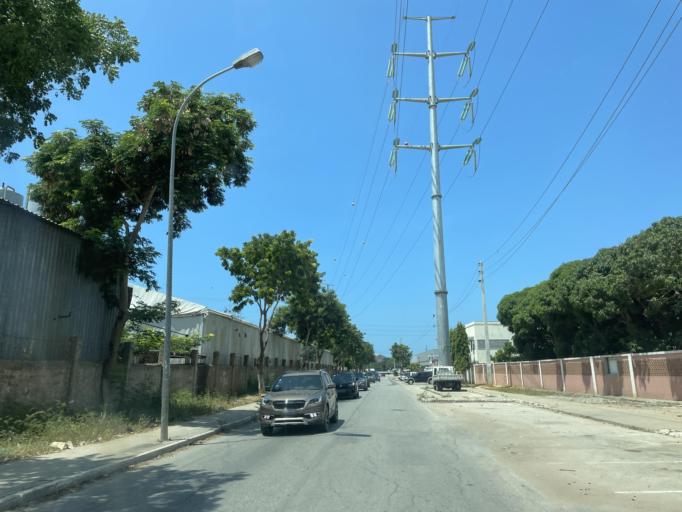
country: AO
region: Luanda
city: Luanda
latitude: -8.9060
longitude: 13.1940
